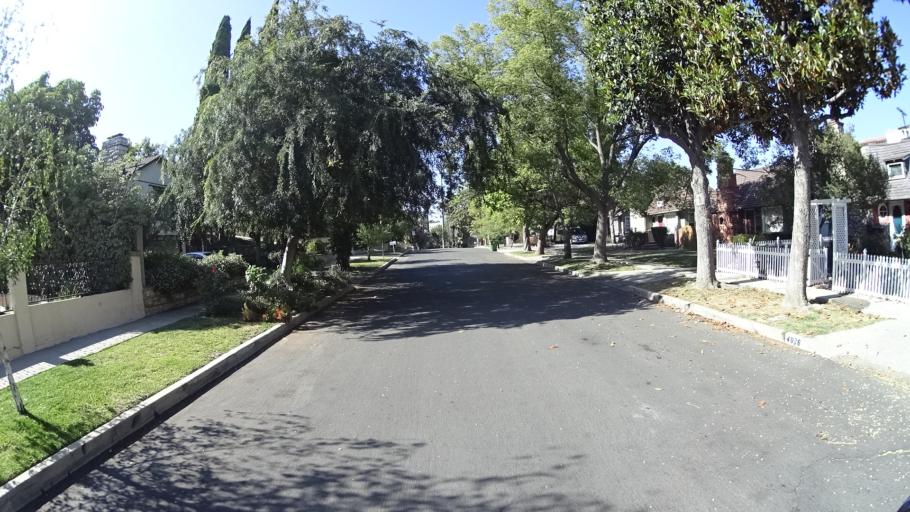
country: US
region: California
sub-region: Los Angeles County
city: Universal City
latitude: 34.1423
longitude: -118.3629
